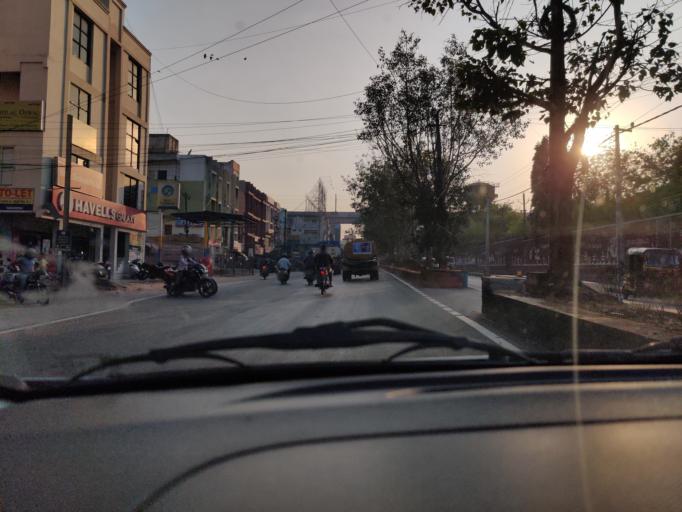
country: IN
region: Telangana
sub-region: Rangareddi
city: Uppal Kalan
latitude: 17.4202
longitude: 78.5428
